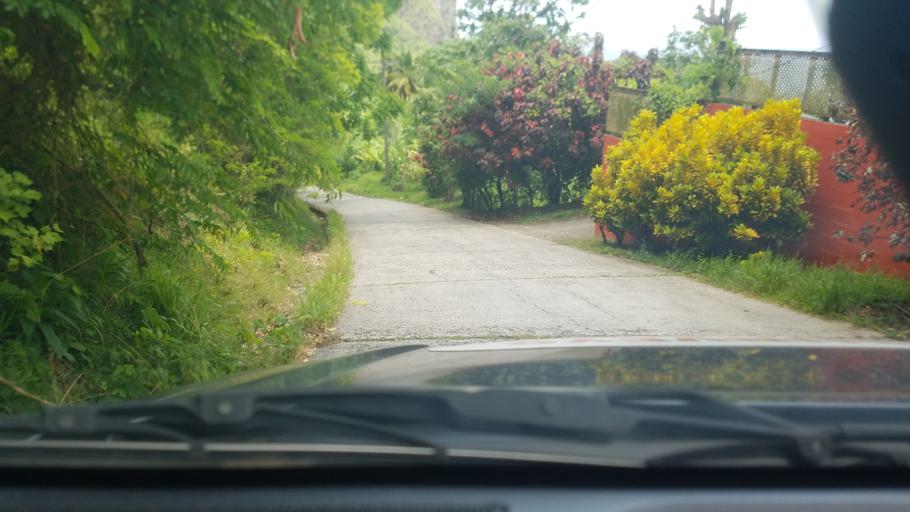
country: LC
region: Soufriere
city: Soufriere
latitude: 13.8438
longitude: -61.0580
